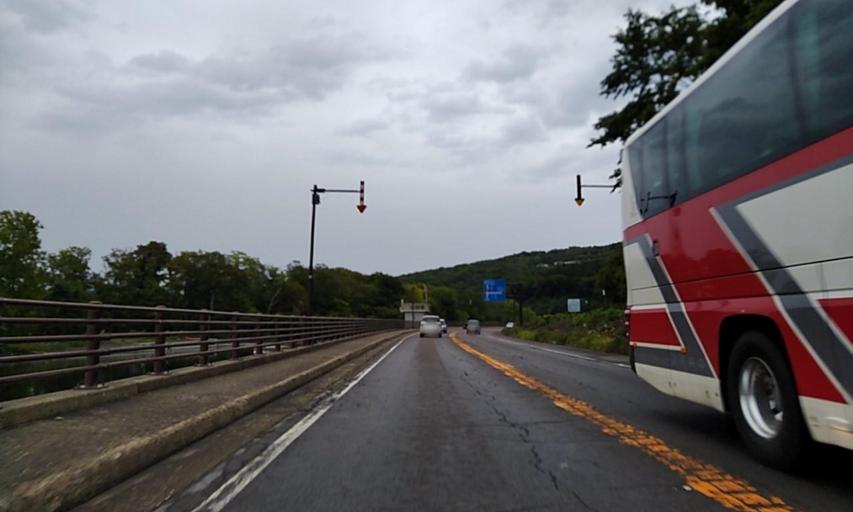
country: JP
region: Hokkaido
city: Abashiri
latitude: 44.0023
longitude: 144.2257
